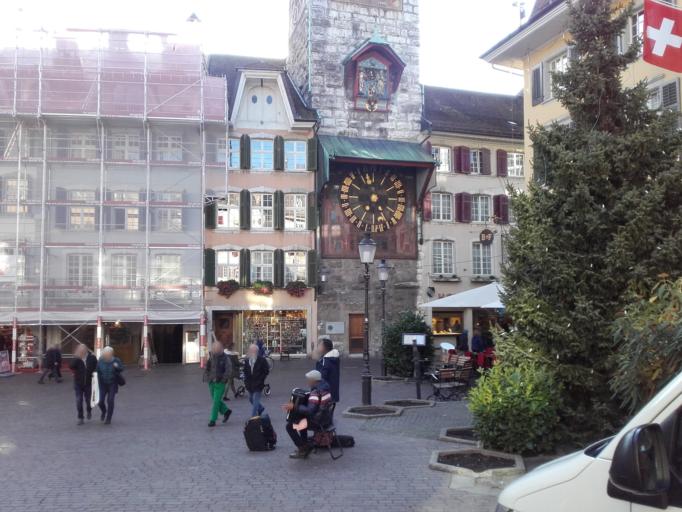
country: CH
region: Solothurn
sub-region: Bezirk Solothurn
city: Solothurn
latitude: 47.2080
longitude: 7.5369
